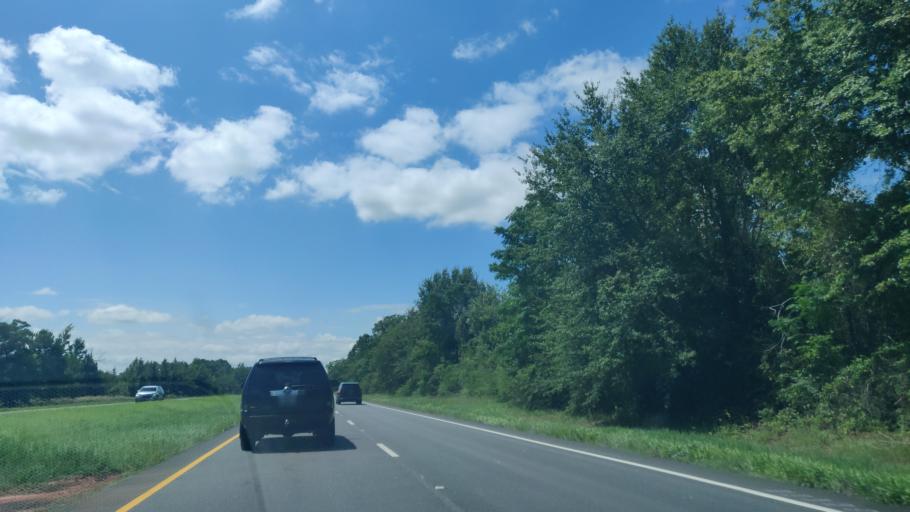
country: US
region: Georgia
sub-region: Stewart County
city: Richland
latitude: 32.1186
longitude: -84.6781
